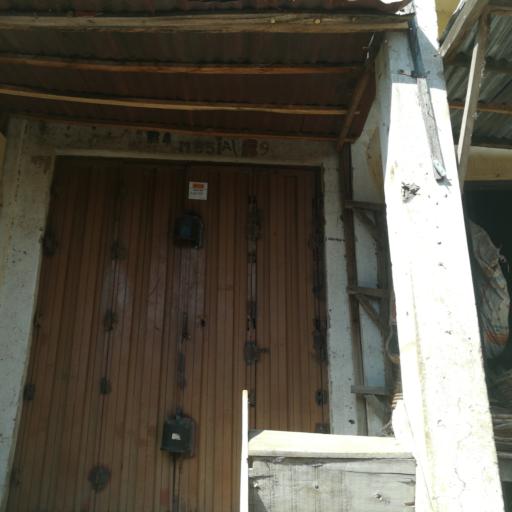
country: NG
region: Kano
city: Kano
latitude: 12.0136
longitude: 8.5354
